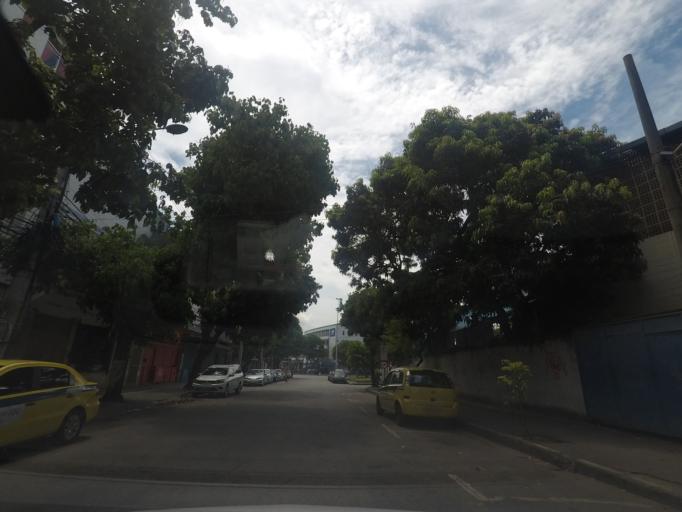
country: BR
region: Rio de Janeiro
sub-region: Rio De Janeiro
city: Rio de Janeiro
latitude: -22.9114
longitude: -43.2123
